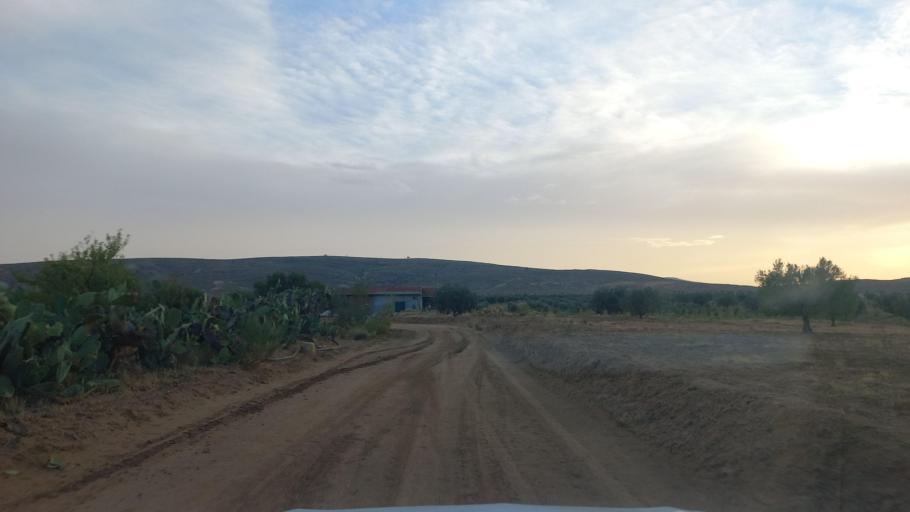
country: TN
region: Al Qasrayn
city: Kasserine
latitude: 35.1890
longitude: 9.0481
